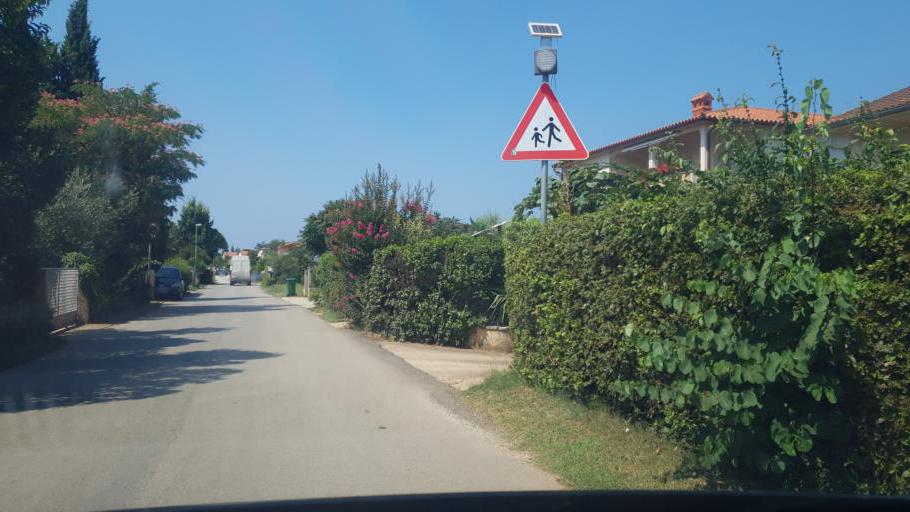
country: HR
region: Istarska
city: Fazana
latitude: 44.9147
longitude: 13.8238
